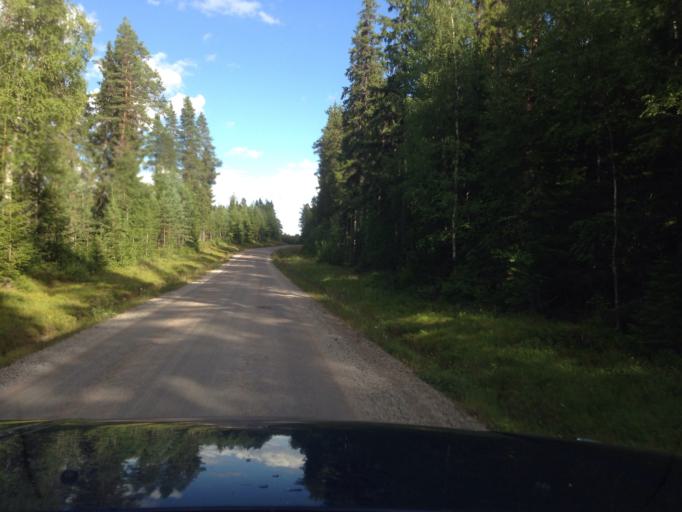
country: SE
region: Dalarna
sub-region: Ludvika Kommun
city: Abborrberget
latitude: 60.3097
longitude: 14.5949
